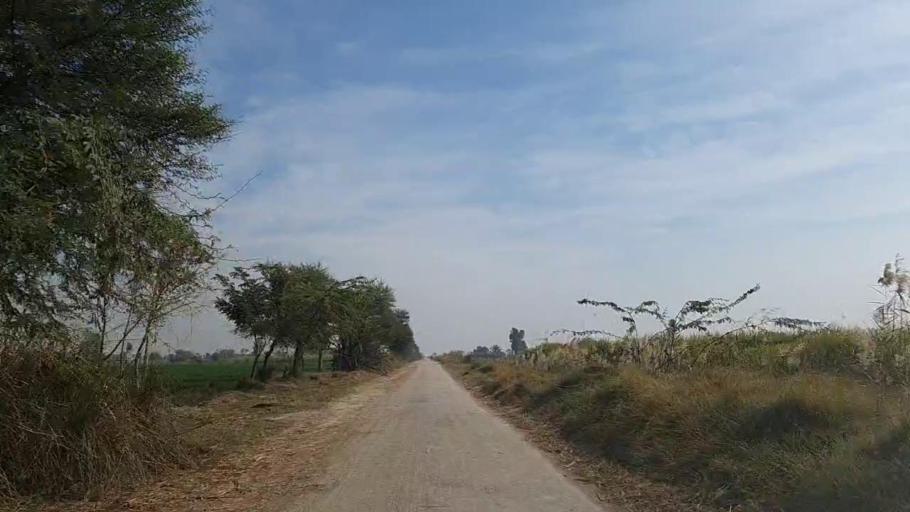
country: PK
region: Sindh
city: Nawabshah
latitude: 26.3321
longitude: 68.4389
